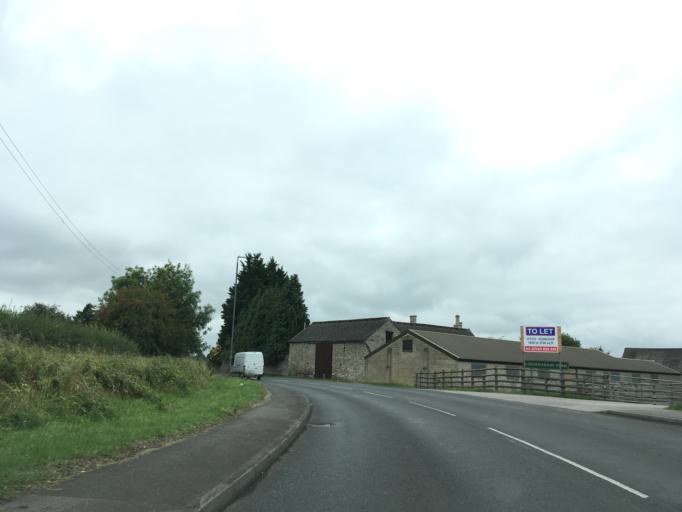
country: GB
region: England
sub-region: Bath and North East Somerset
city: Keynsham
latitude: 51.4278
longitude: -2.4838
